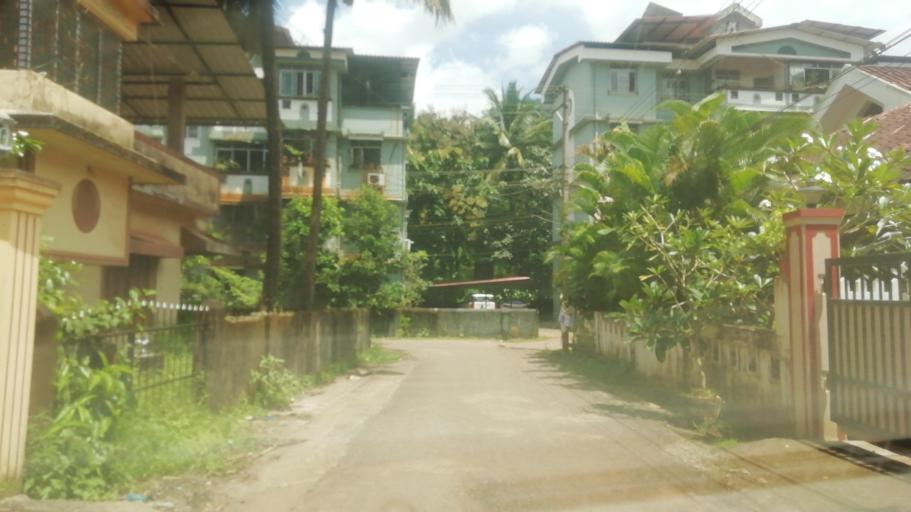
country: IN
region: Goa
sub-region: North Goa
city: Ponda
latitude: 15.3952
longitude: 74.0093
